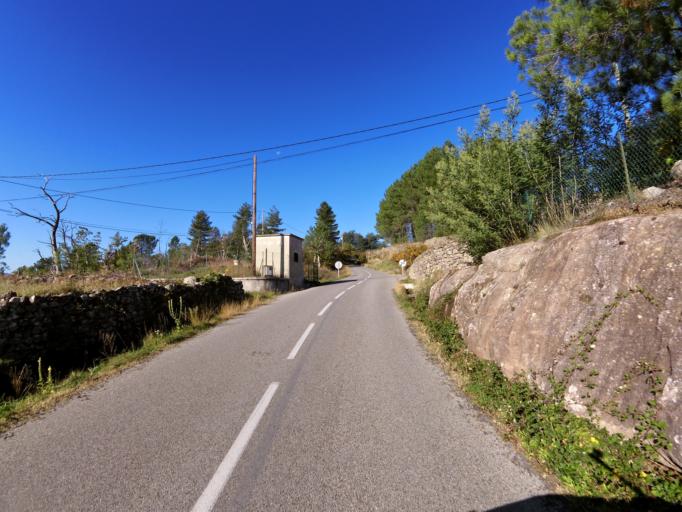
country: FR
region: Rhone-Alpes
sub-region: Departement de l'Ardeche
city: Lablachere
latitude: 44.4809
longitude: 4.1668
